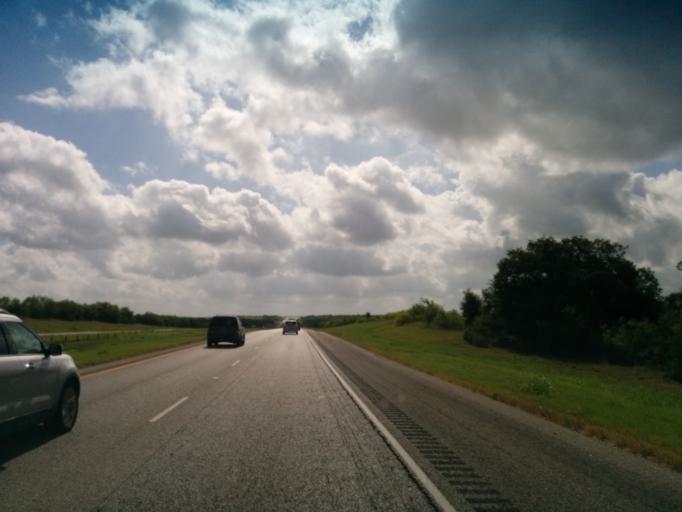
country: US
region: Texas
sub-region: Gonzales County
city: Waelder
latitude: 29.6647
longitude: -97.3561
